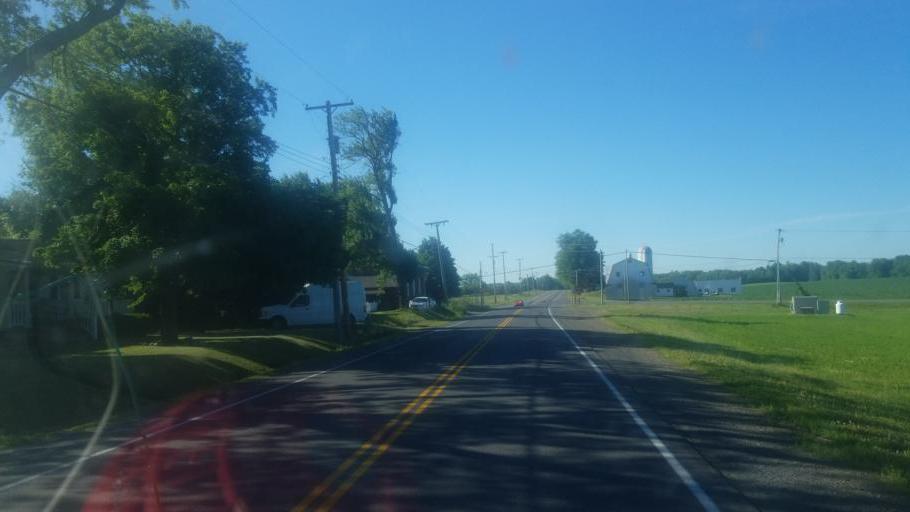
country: US
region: New York
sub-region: Ontario County
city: Phelps
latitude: 42.9177
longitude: -77.0632
